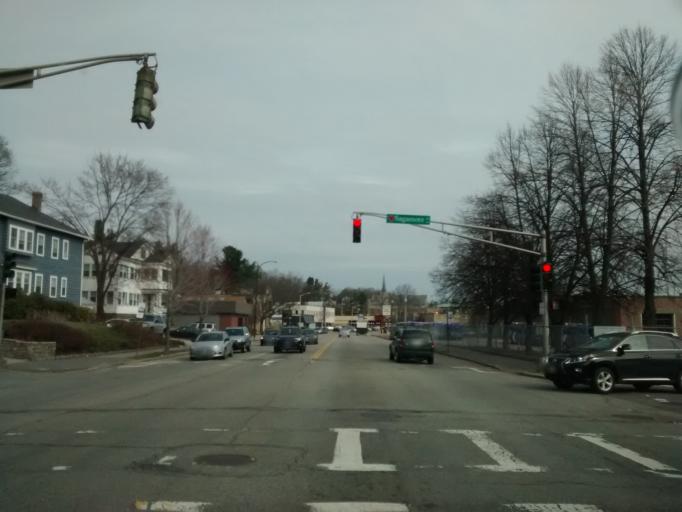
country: US
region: Massachusetts
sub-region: Worcester County
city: Worcester
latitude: 42.2815
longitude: -71.8086
